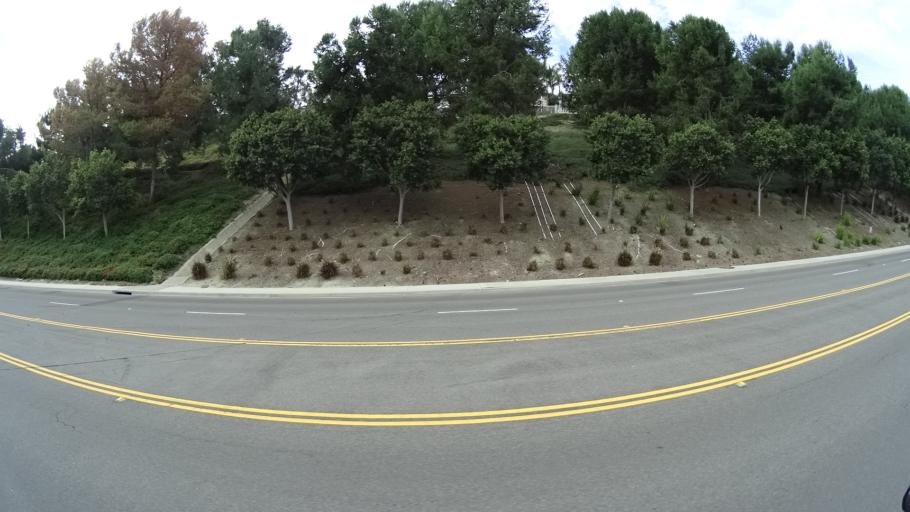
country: US
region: California
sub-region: Orange County
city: Aliso Viejo
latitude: 33.5596
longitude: -117.7293
